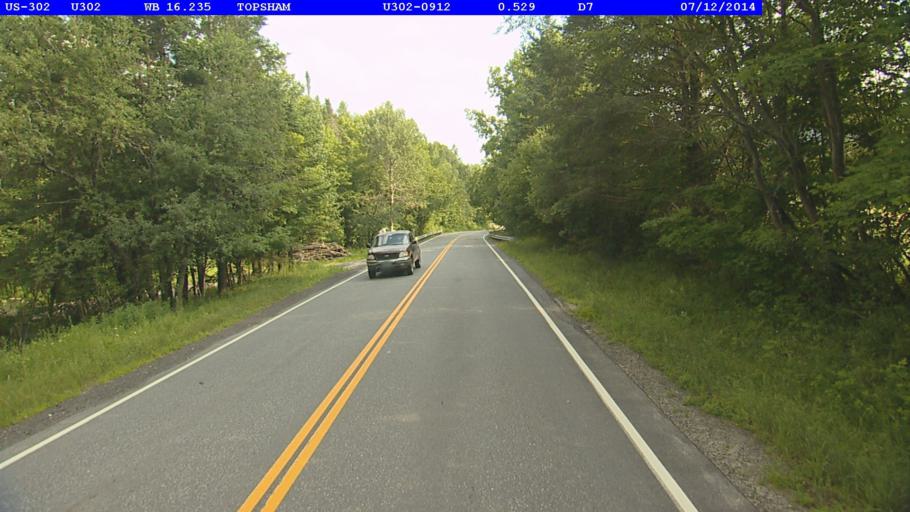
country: US
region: Vermont
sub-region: Washington County
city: South Barre
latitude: 44.1451
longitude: -72.3102
